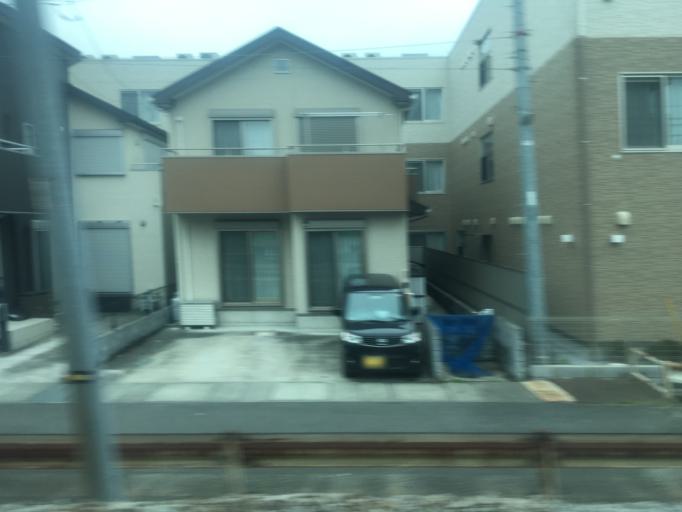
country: JP
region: Saitama
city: Ageoshimo
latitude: 35.9581
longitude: 139.5995
